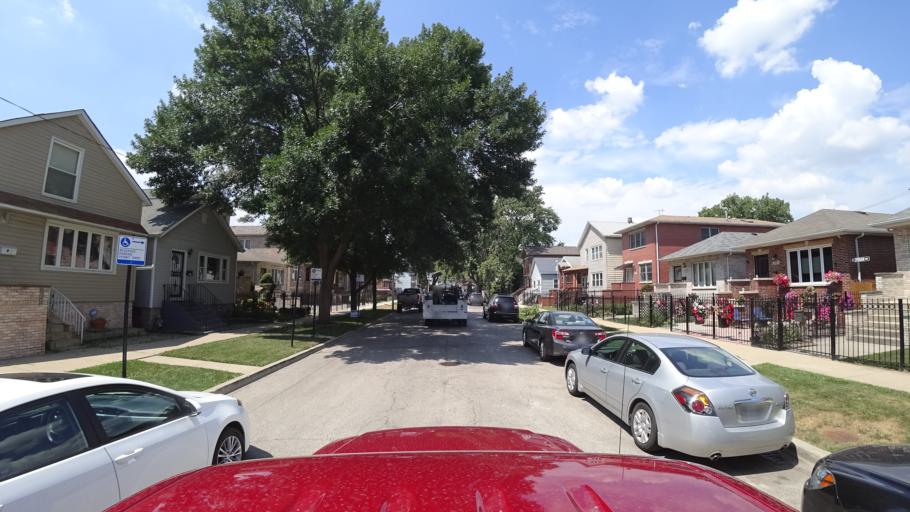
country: US
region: Illinois
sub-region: Cook County
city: Chicago
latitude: 41.8181
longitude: -87.6392
